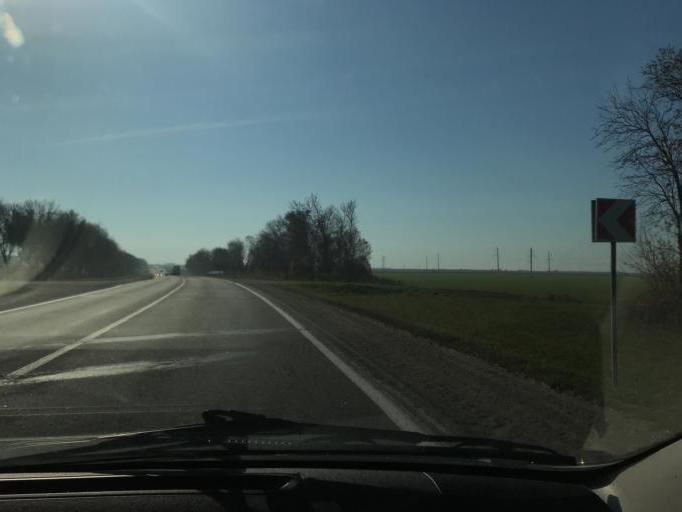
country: BY
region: Minsk
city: Salihorsk
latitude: 52.8786
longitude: 27.4678
